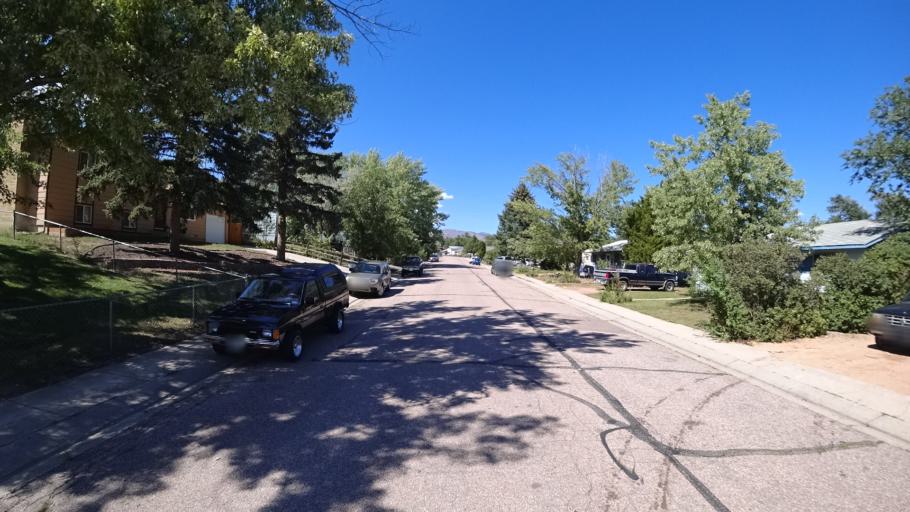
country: US
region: Colorado
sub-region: El Paso County
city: Colorado Springs
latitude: 38.8584
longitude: -104.8521
